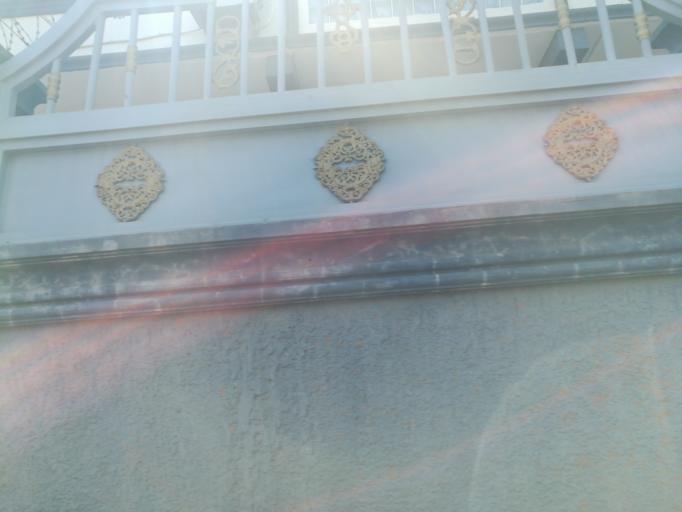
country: NG
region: Abuja Federal Capital Territory
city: Abuja
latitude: 9.0735
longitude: 7.4497
